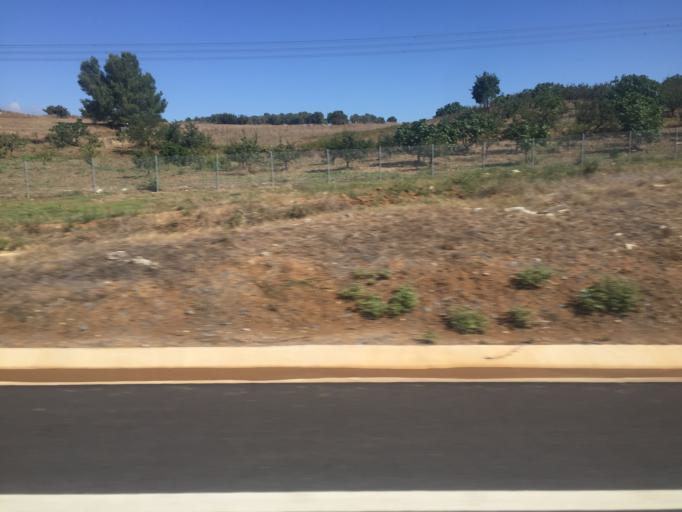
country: TR
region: Bursa
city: Mahmudiye
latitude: 40.2750
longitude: 28.5736
